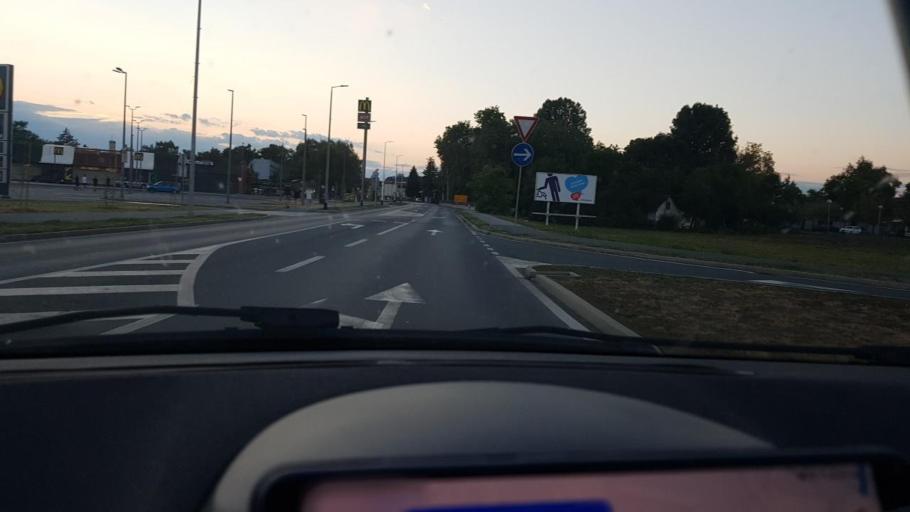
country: HR
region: Bjelovarsko-Bilogorska
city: Bjelovar
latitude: 45.8912
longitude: 16.8542
